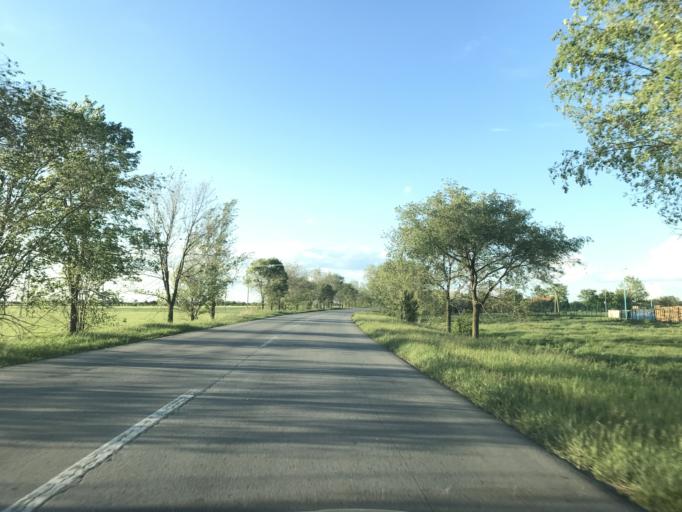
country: RS
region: Autonomna Pokrajina Vojvodina
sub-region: Srednjebanatski Okrug
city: Zrenjanin
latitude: 45.3897
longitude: 20.3526
